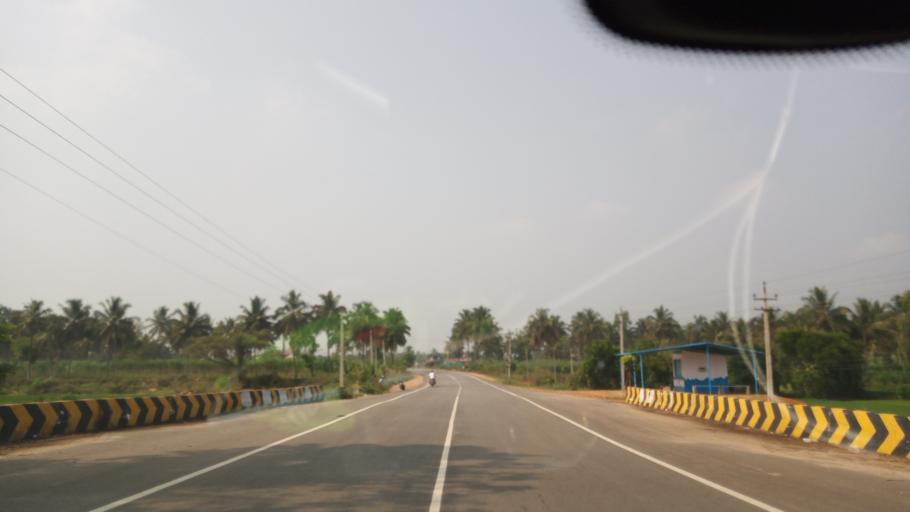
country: IN
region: Karnataka
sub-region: Mandya
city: Pandavapura
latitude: 12.5420
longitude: 76.6705
